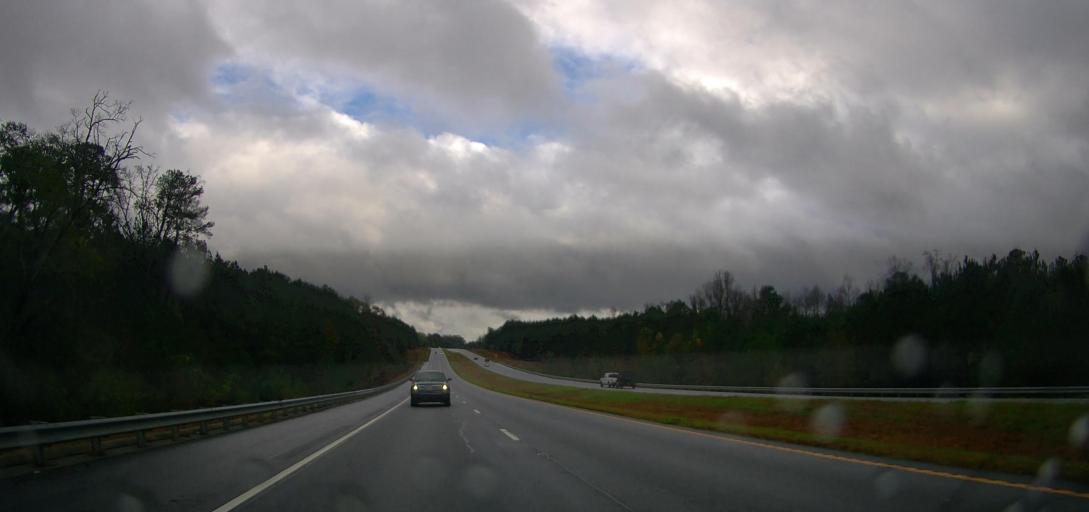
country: US
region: Georgia
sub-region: Jackson County
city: Nicholson
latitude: 34.0918
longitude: -83.4279
